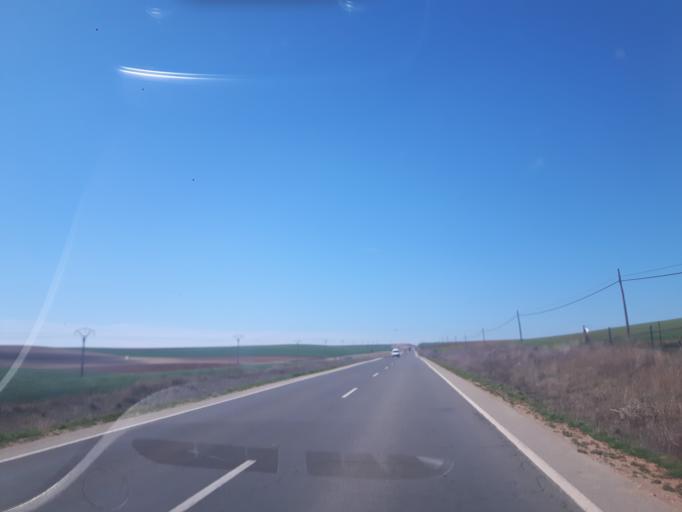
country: ES
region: Castille and Leon
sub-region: Provincia de Salamanca
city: Aldeaseca de Alba
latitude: 40.8370
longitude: -5.4757
